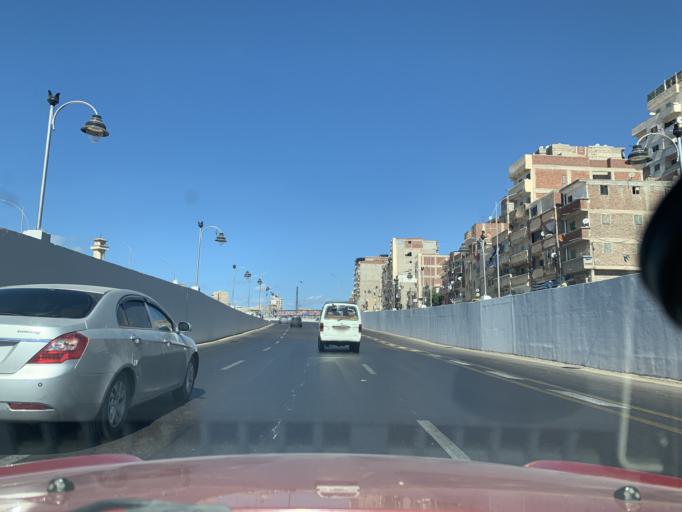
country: EG
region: Alexandria
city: Alexandria
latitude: 31.2174
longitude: 29.9638
